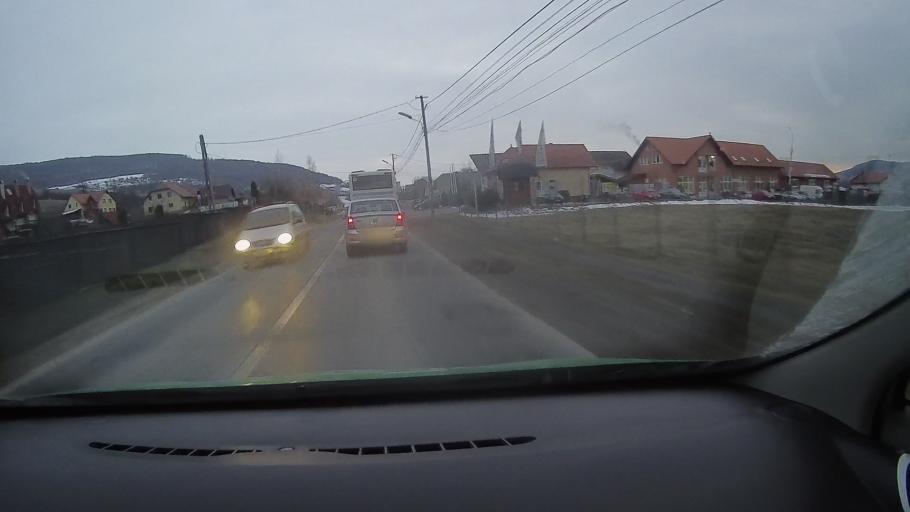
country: RO
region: Harghita
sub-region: Municipiul Odorheiu Secuiesc
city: Odorheiu Secuiesc
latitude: 46.2863
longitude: 25.2898
